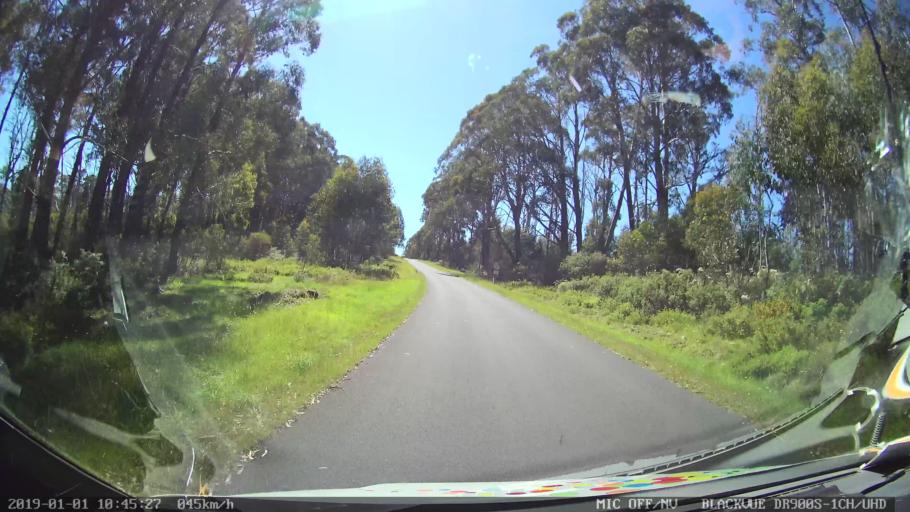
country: AU
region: New South Wales
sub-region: Snowy River
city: Jindabyne
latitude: -36.0358
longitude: 148.3375
